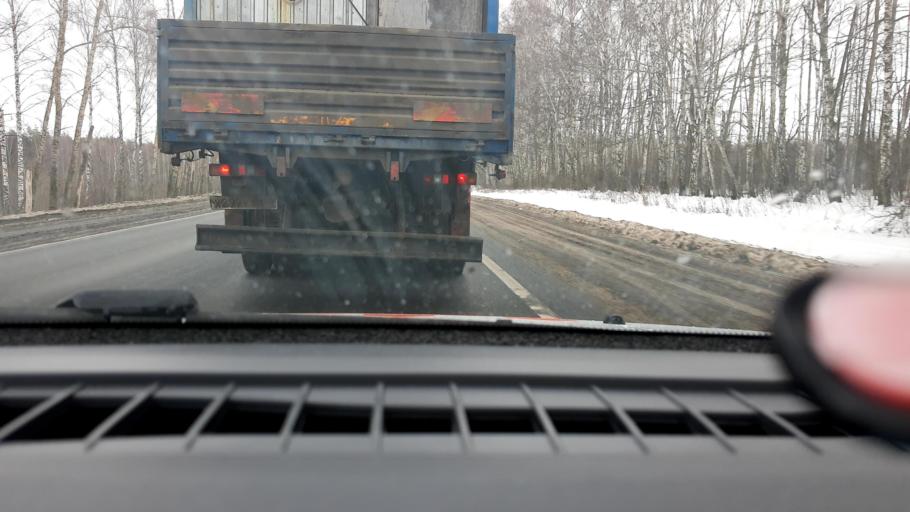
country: RU
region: Nizjnij Novgorod
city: Pamyat' Parizhskoy Kommuny
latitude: 56.0291
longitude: 44.5367
